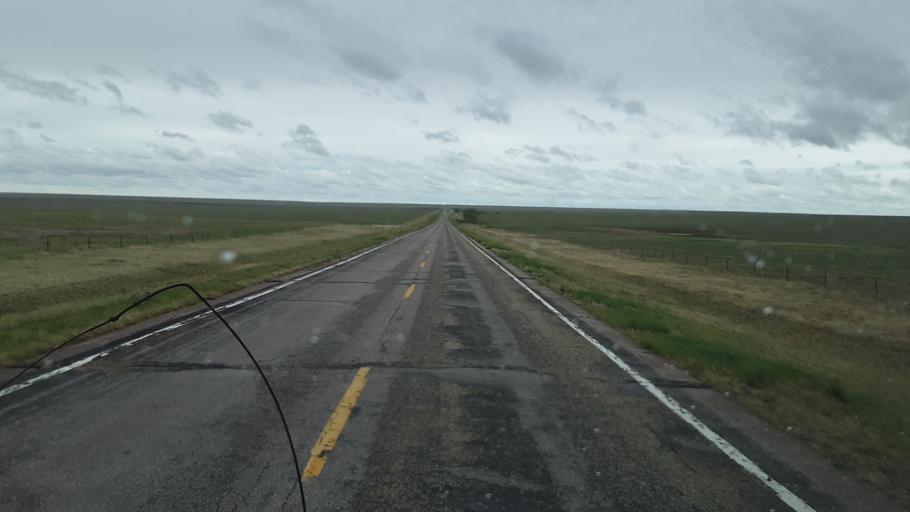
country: US
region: Colorado
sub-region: Lincoln County
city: Hugo
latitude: 38.8497
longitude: -103.3191
